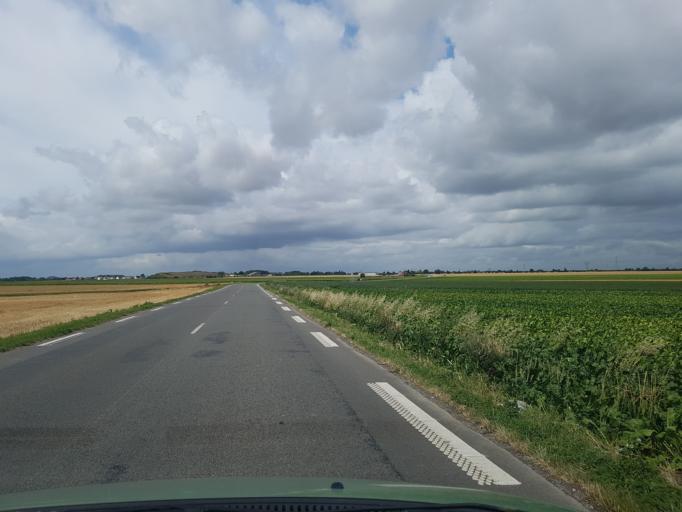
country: FR
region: Nord-Pas-de-Calais
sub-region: Departement du Pas-de-Calais
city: Vermelles
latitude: 50.4855
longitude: 2.7755
